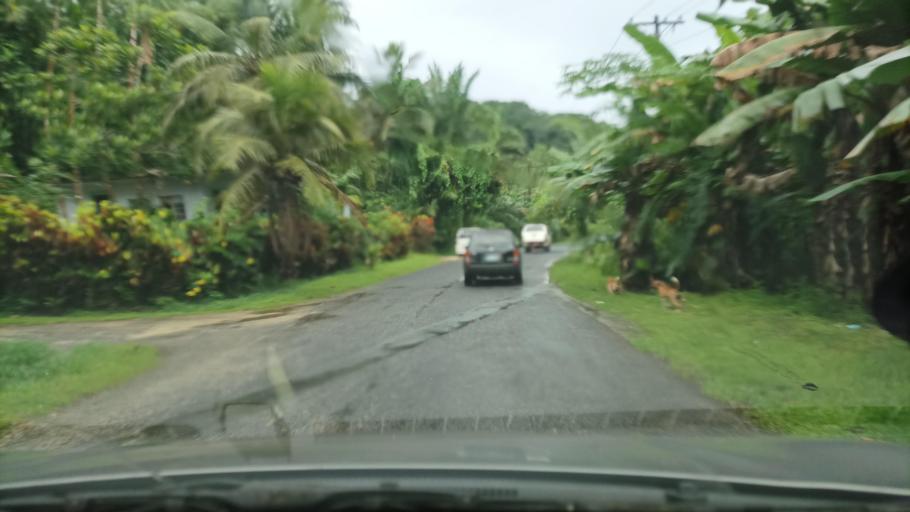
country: FM
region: Pohnpei
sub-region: Sokehs Municipality
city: Palikir - National Government Center
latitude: 6.8437
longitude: 158.1571
